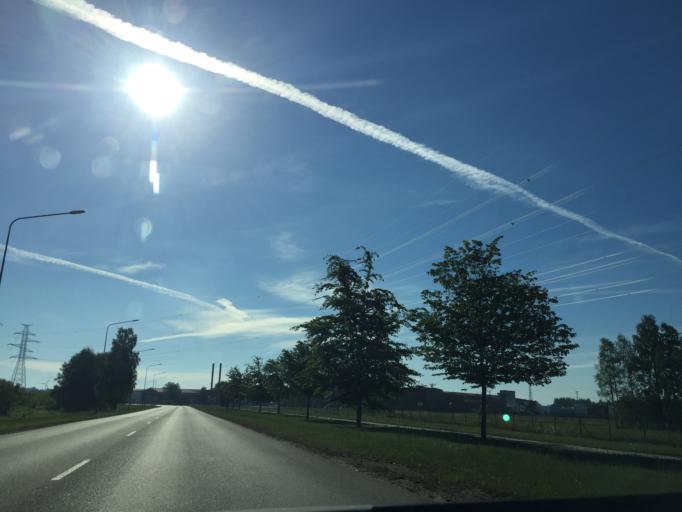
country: LV
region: Ventspils
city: Ventspils
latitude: 57.3969
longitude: 21.6429
